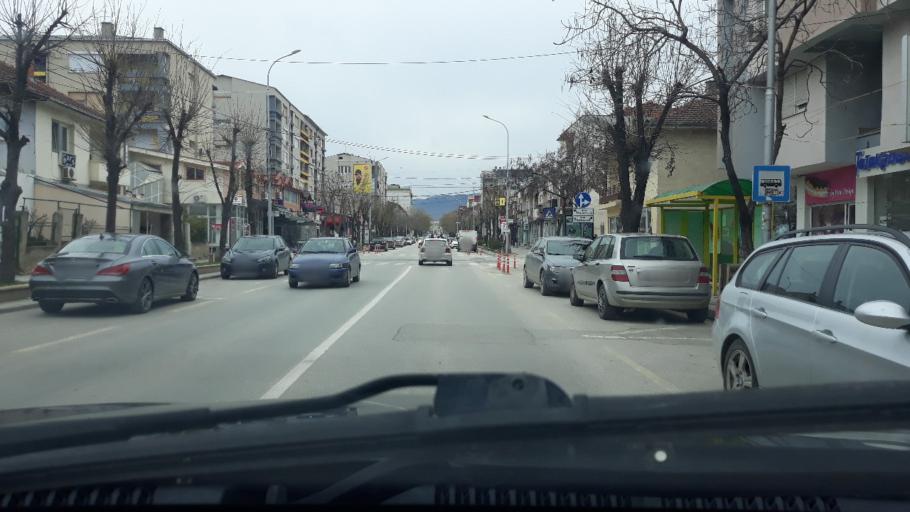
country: MK
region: Kavadarci
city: Kavadarci
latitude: 41.4381
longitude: 22.0105
